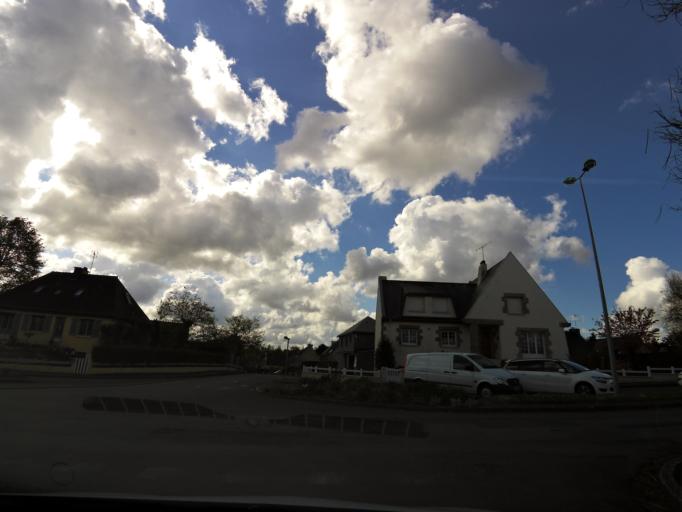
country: FR
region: Brittany
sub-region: Departement d'Ille-et-Vilaine
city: Saint-Erblon
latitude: 48.0177
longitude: -1.6511
